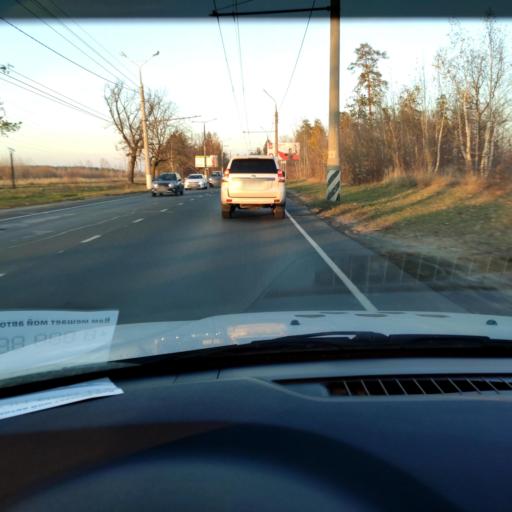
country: RU
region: Samara
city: Tol'yatti
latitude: 53.4869
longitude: 49.3823
